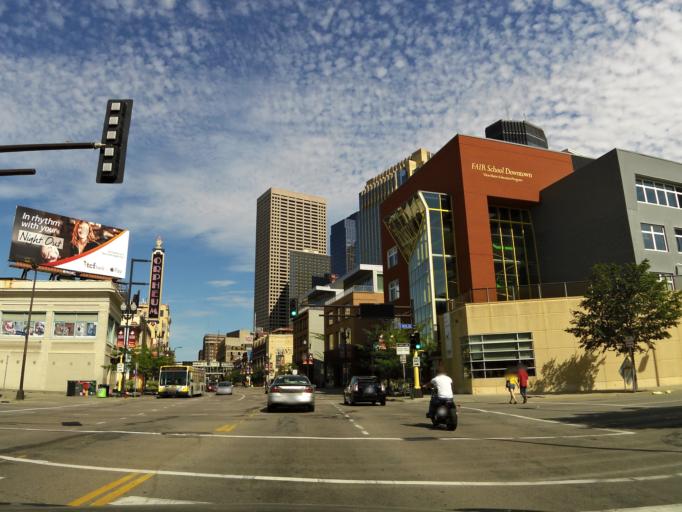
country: US
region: Minnesota
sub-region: Hennepin County
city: Minneapolis
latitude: 44.9756
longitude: -93.2783
